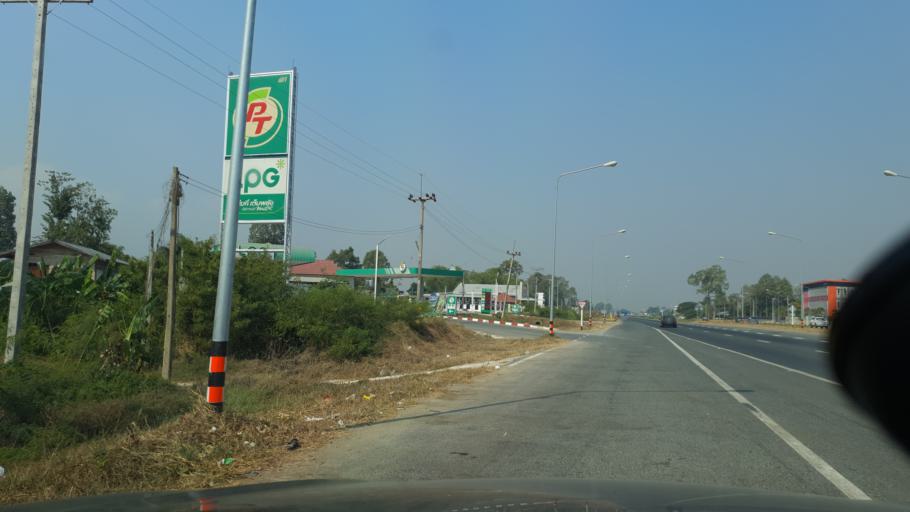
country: TH
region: Nakhon Sawan
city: Nakhon Sawan
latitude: 15.6546
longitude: 100.0761
